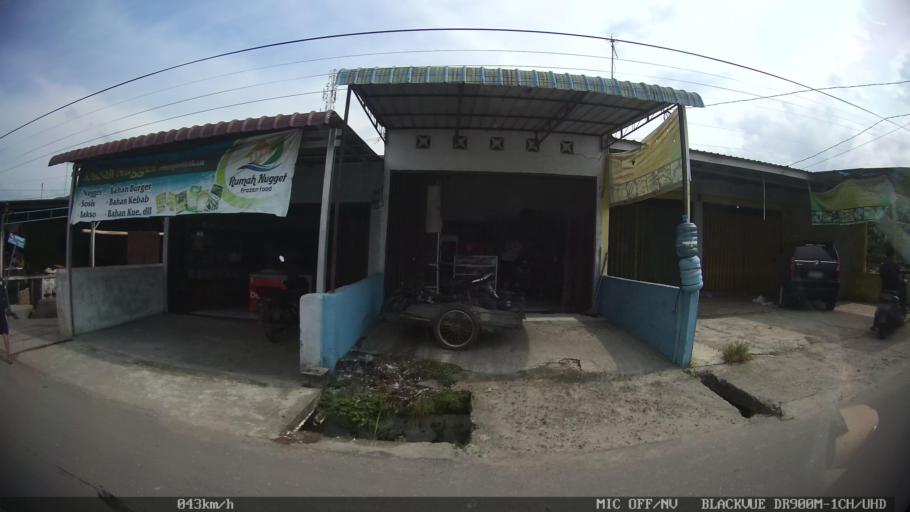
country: ID
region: North Sumatra
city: Percut
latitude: 3.6071
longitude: 98.7695
